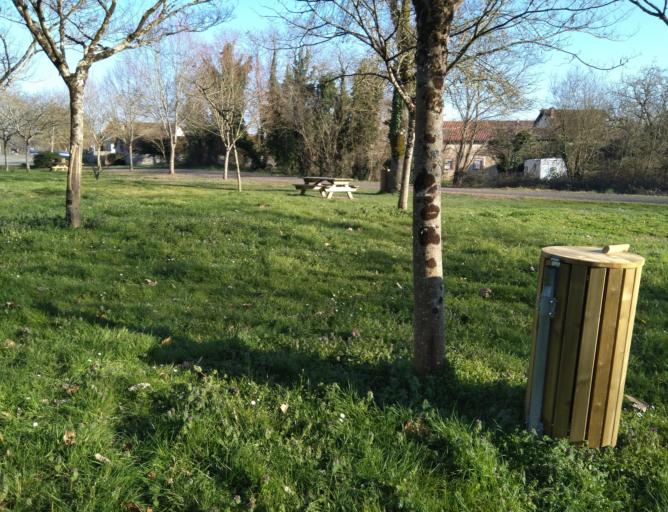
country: FR
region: Midi-Pyrenees
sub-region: Departement du Gers
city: Riscle
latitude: 43.6634
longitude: -0.0839
